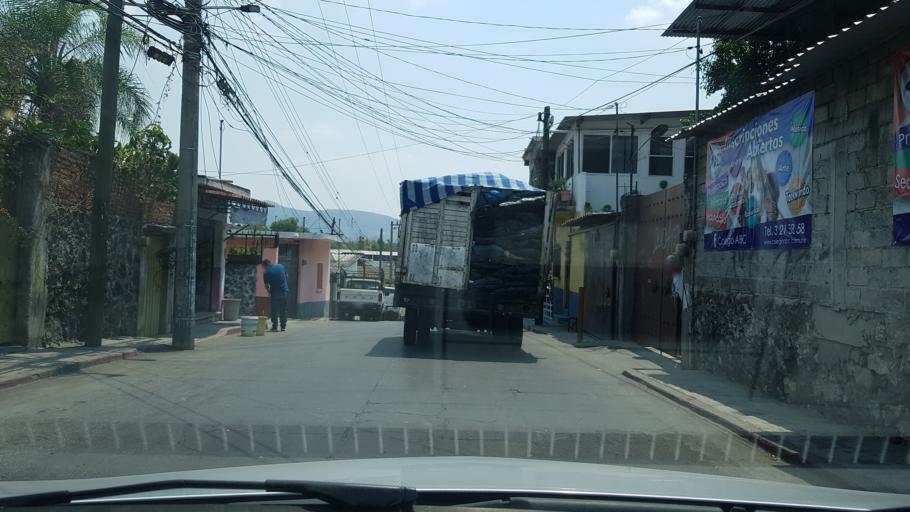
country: MX
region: Morelos
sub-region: Jiutepec
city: Jiutepec
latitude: 18.8788
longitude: -99.1788
